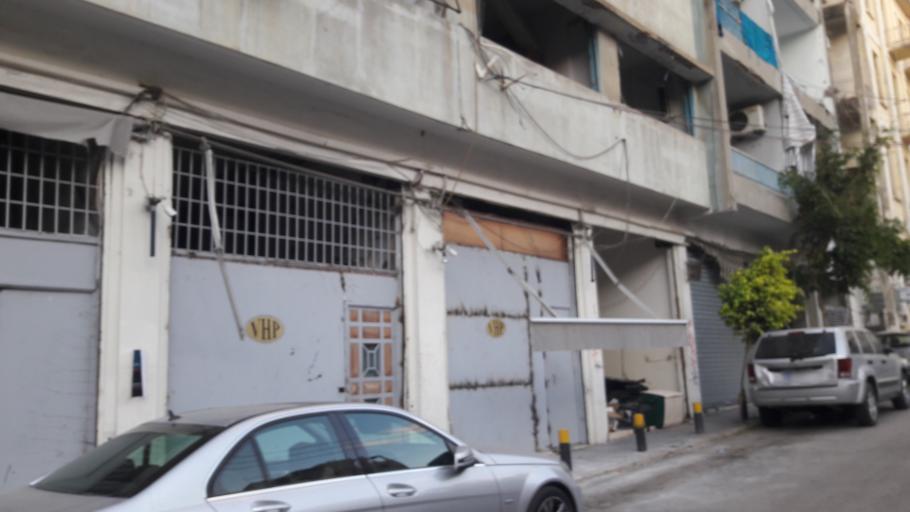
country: LB
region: Beyrouth
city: Beirut
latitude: 33.8977
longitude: 35.5260
